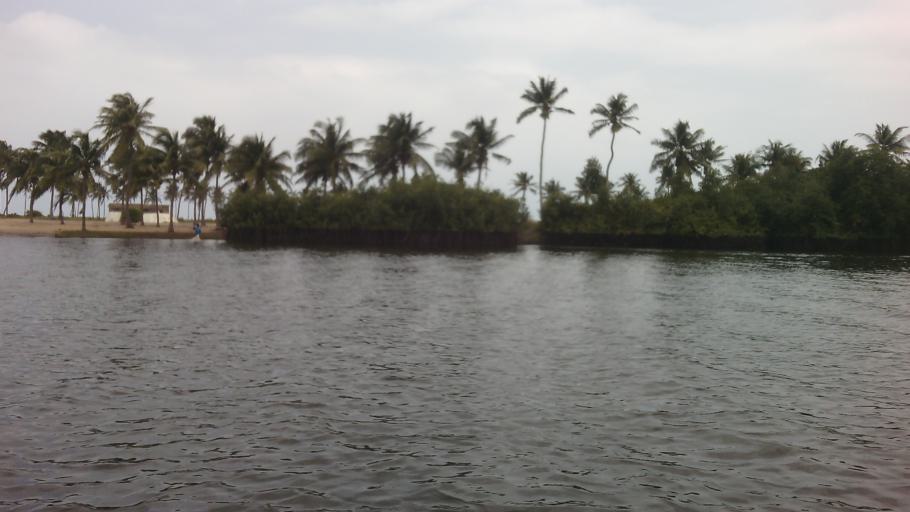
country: BJ
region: Atlantique
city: Ouidah
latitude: 6.3078
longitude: 1.9866
